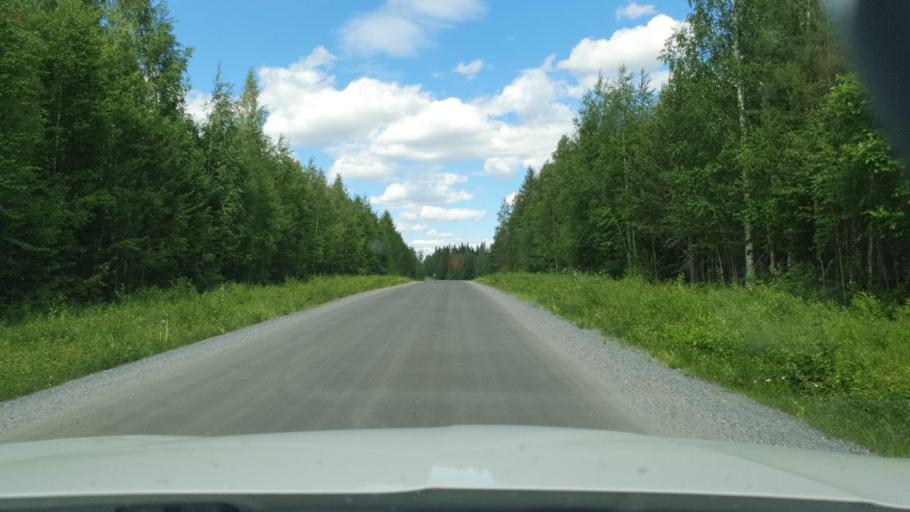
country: SE
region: Vaesterbotten
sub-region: Skelleftea Kommun
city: Forsbacka
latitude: 64.8189
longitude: 20.4948
